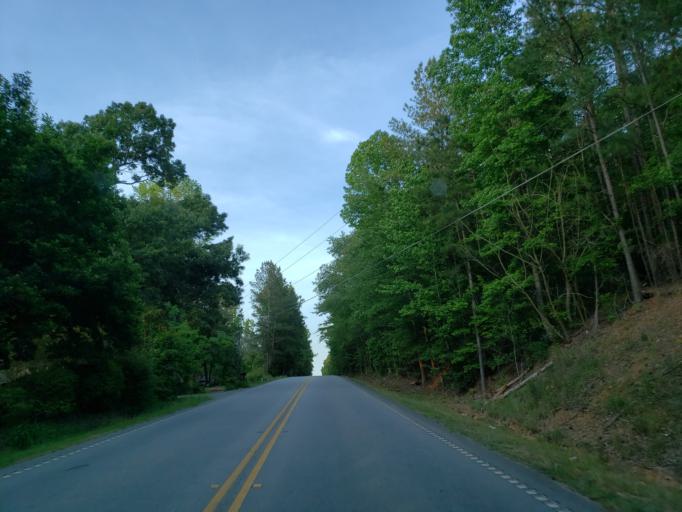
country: US
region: Georgia
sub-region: Fulton County
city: Chattahoochee Hills
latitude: 33.4968
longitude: -84.9052
